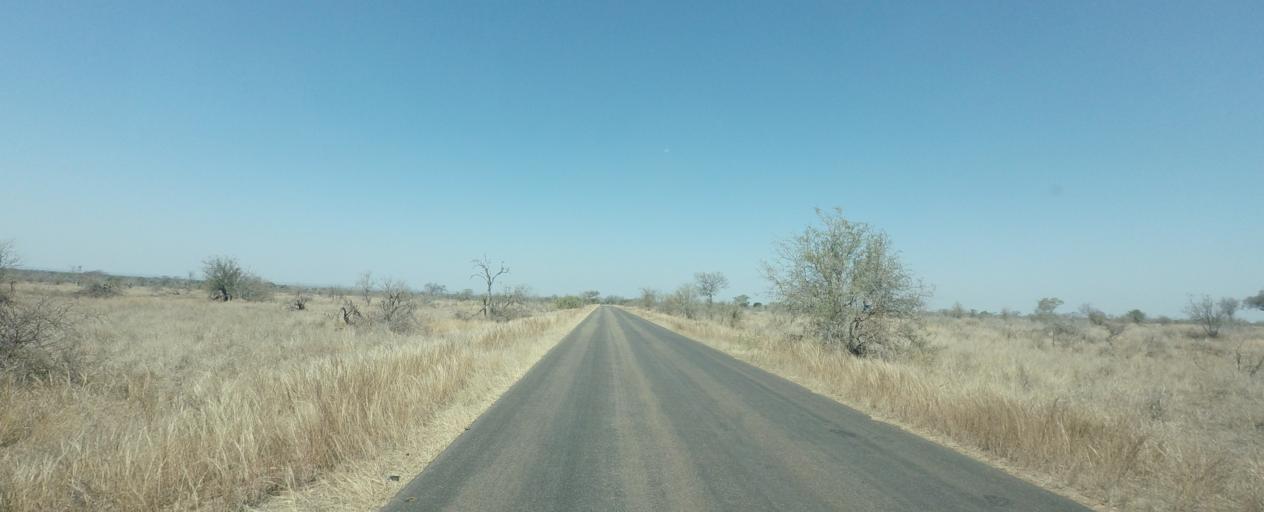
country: ZA
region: Limpopo
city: Thulamahashi
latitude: -24.4026
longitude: 31.7621
